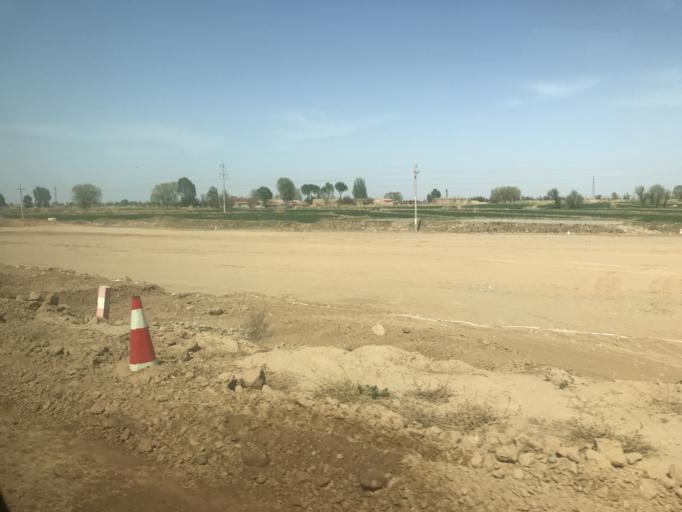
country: CN
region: Gansu Sheng
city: Gulang
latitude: 37.5352
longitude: 102.8980
